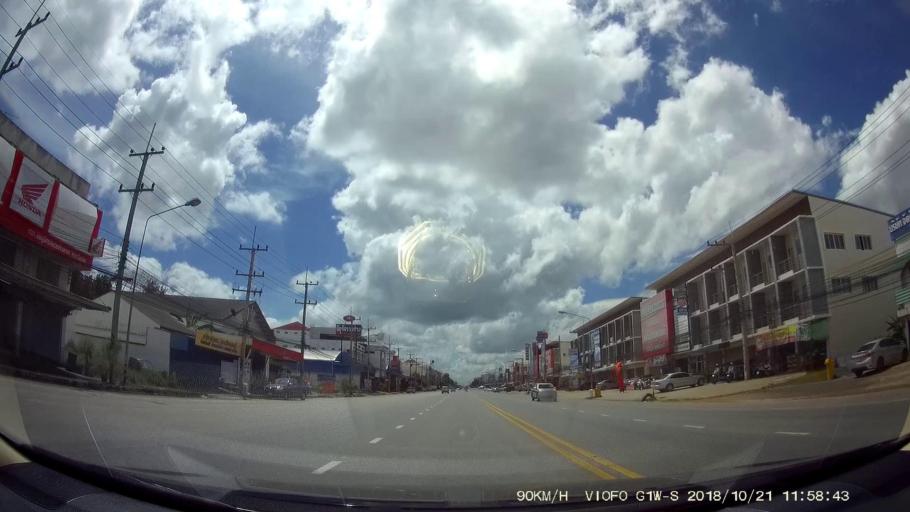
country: TH
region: Chaiyaphum
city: Chatturat
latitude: 15.5673
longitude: 101.8516
